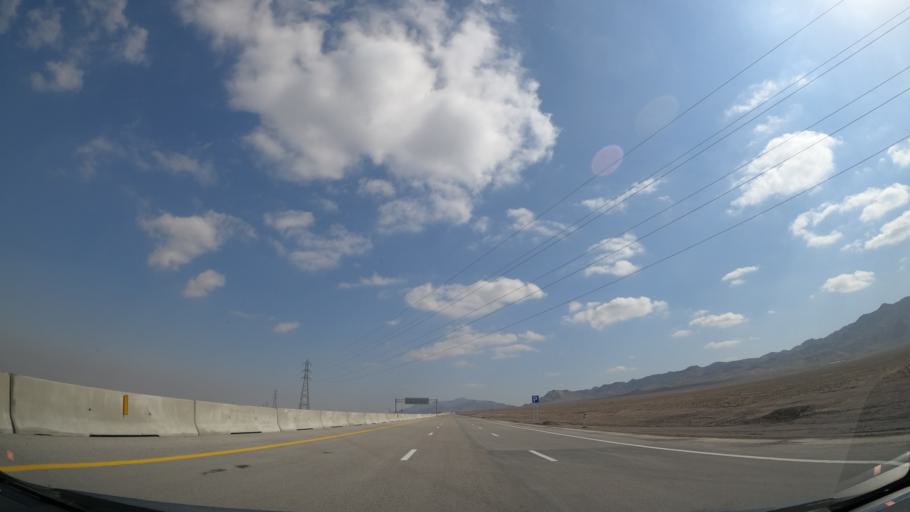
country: IR
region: Alborz
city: Eshtehard
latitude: 35.7160
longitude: 50.5797
